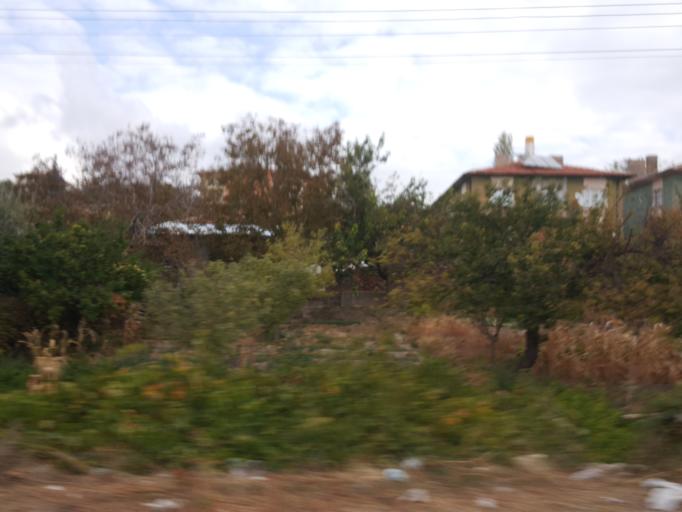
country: TR
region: Kirikkale
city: Keskin
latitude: 39.6730
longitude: 33.6066
